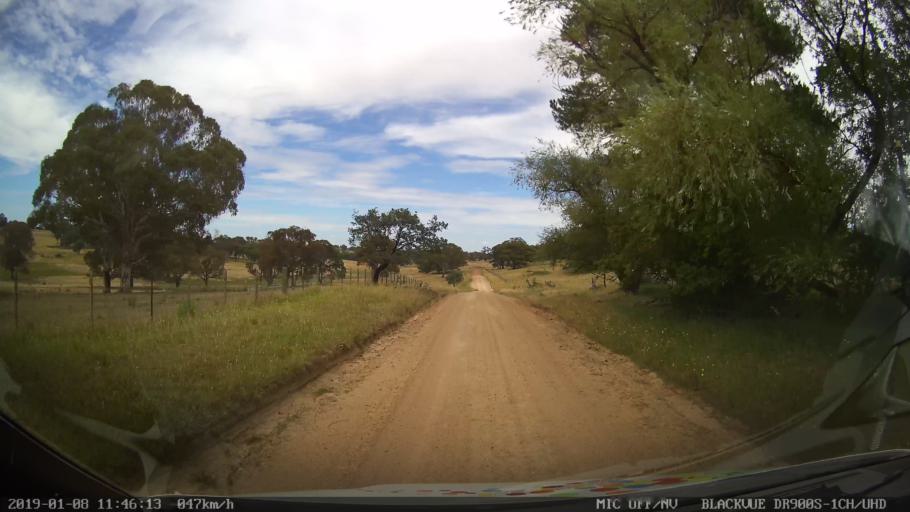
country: AU
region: New South Wales
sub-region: Armidale Dumaresq
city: Armidale
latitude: -30.3809
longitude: 151.5841
